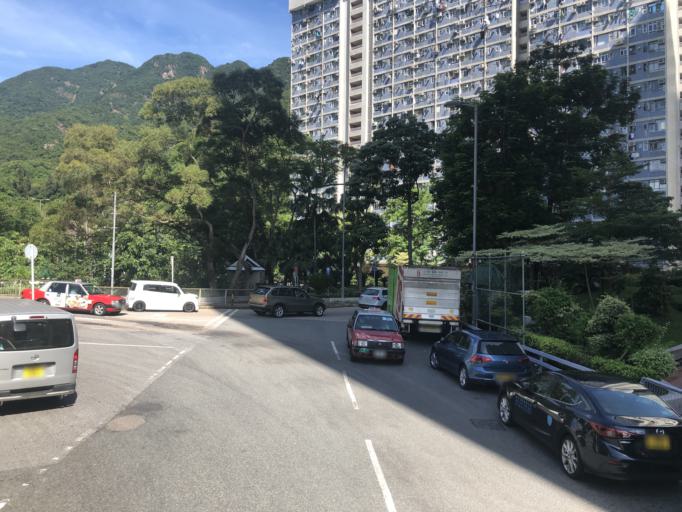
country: HK
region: Sai Kung
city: Sai Kung
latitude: 22.4180
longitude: 114.2294
